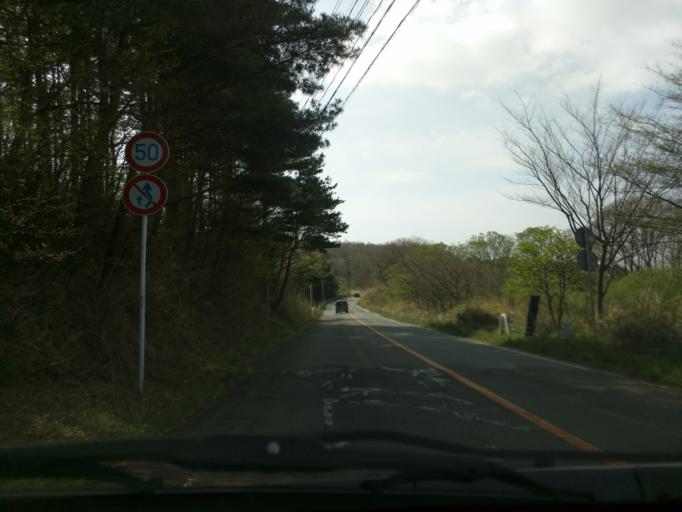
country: JP
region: Fukushima
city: Nihommatsu
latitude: 37.6007
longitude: 140.3617
